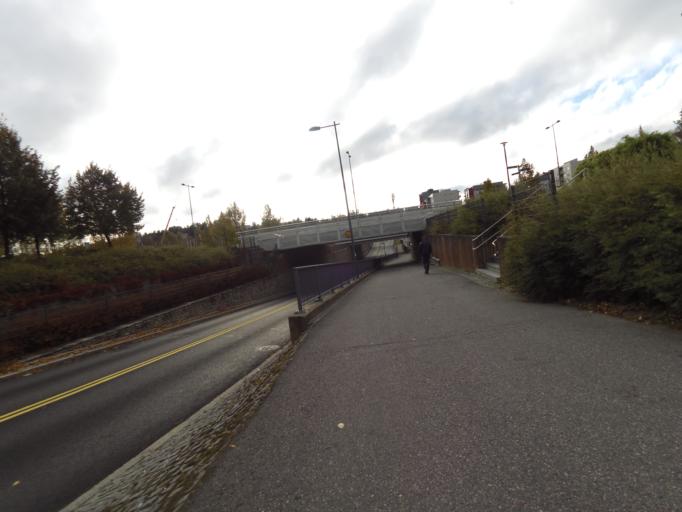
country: FI
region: Uusimaa
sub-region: Helsinki
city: Espoo
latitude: 60.2068
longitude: 24.6605
